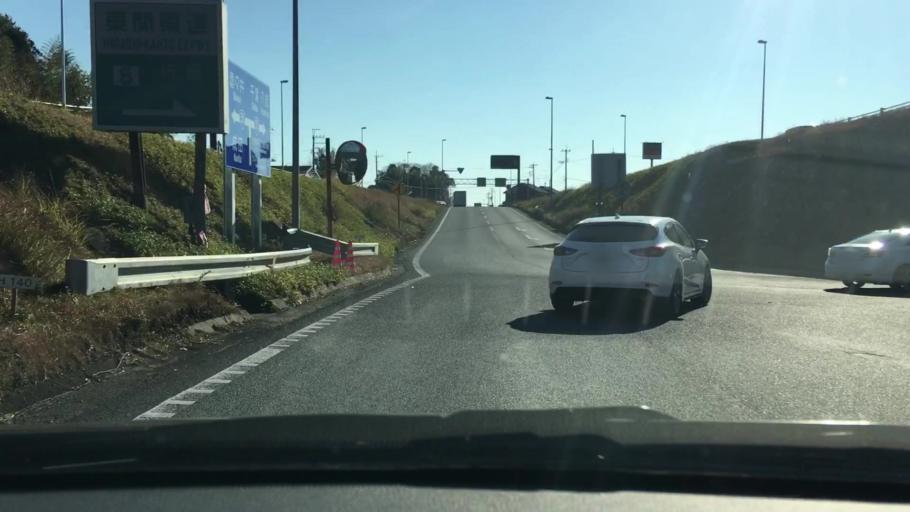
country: JP
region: Chiba
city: Sakura
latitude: 35.6864
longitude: 140.2425
